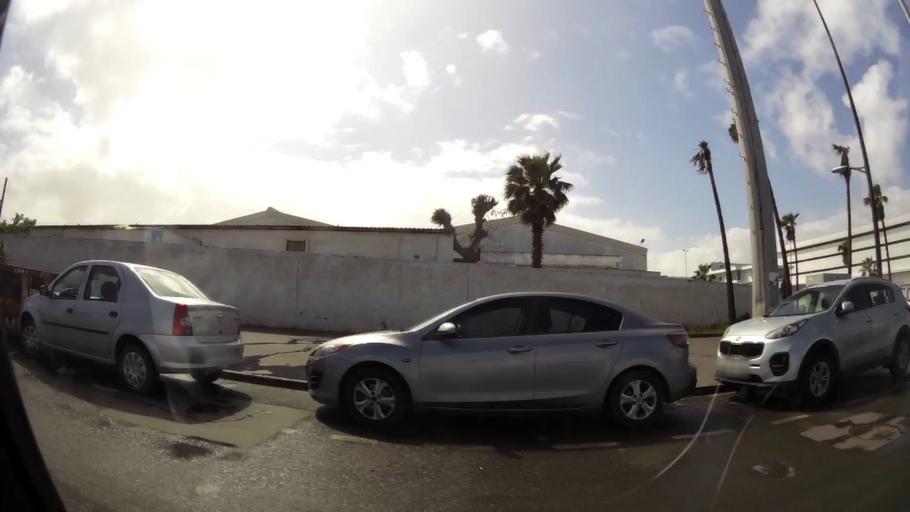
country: MA
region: Grand Casablanca
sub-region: Casablanca
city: Casablanca
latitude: 33.6157
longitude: -7.5516
